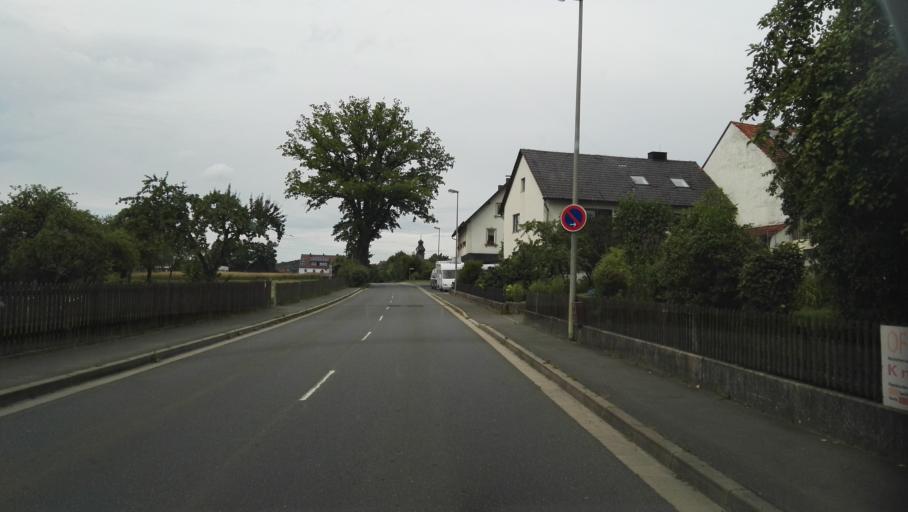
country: DE
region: Bavaria
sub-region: Upper Franconia
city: Plankenfels
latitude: 49.8848
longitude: 11.3341
